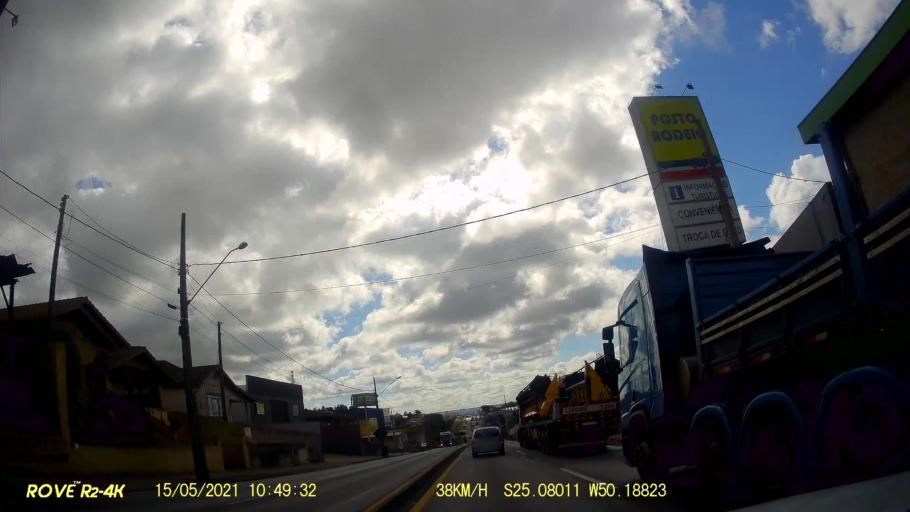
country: BR
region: Parana
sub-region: Ponta Grossa
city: Ponta Grossa
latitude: -25.0795
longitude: -50.1880
